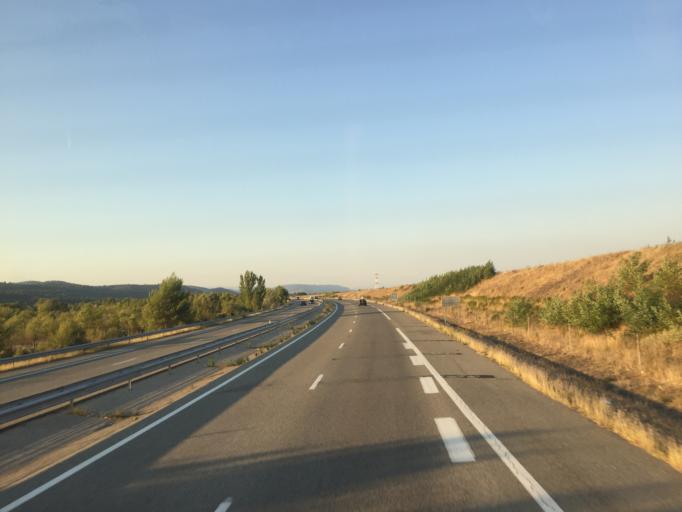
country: FR
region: Provence-Alpes-Cote d'Azur
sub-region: Departement du Vaucluse
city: Beaumont-de-Pertuis
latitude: 43.7088
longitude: 5.7343
